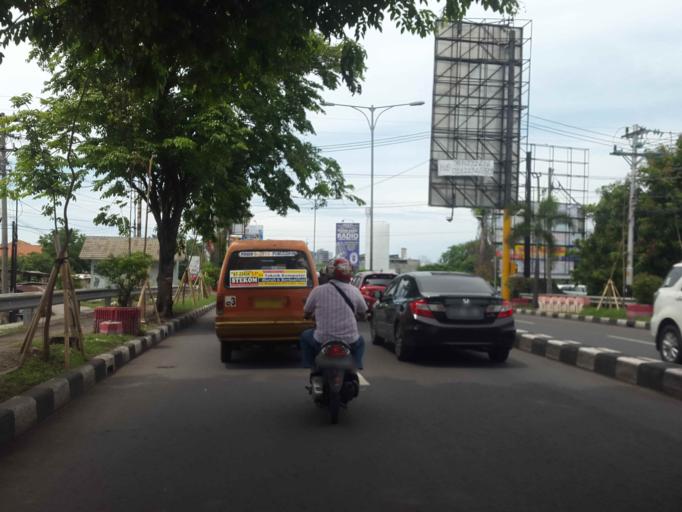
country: ID
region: Central Java
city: Semarang
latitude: -6.9976
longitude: 110.4398
